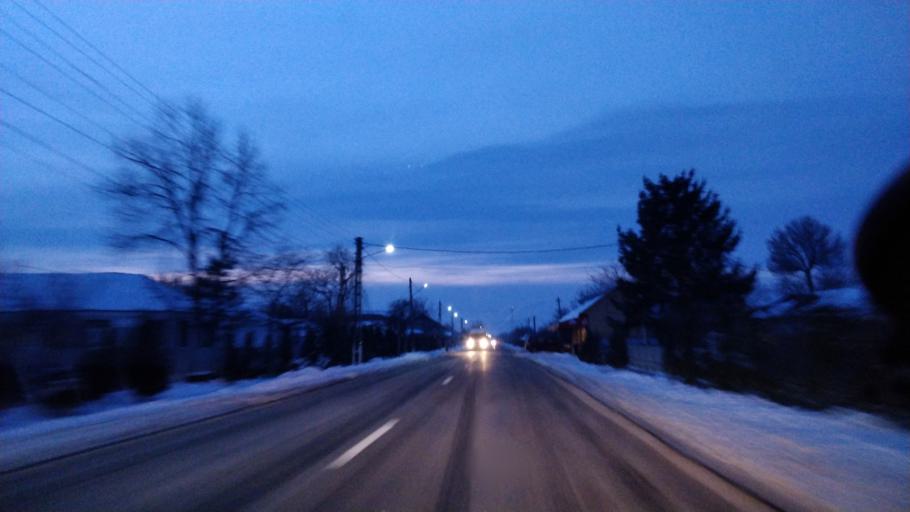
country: RO
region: Vrancea
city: Vulturu de Sus
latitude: 45.6147
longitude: 27.4323
